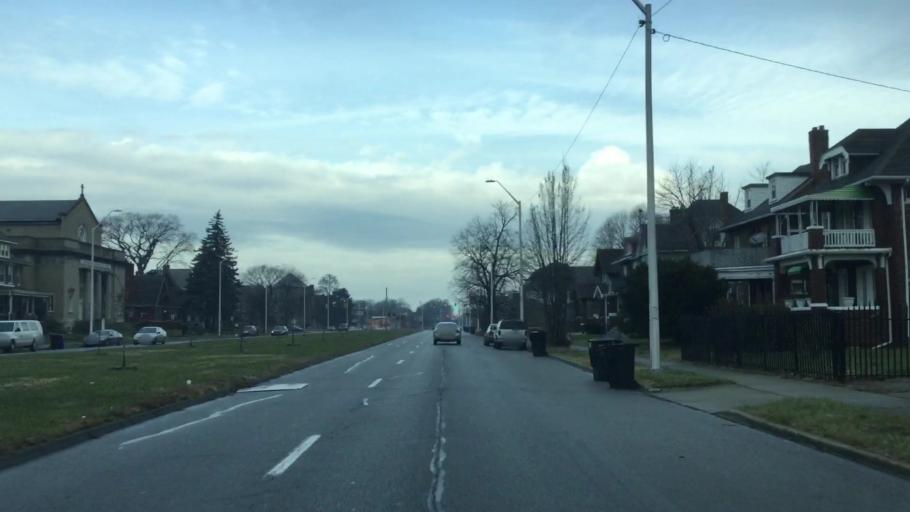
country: US
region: Michigan
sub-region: Wayne County
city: Hamtramck
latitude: 42.3698
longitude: -83.0165
